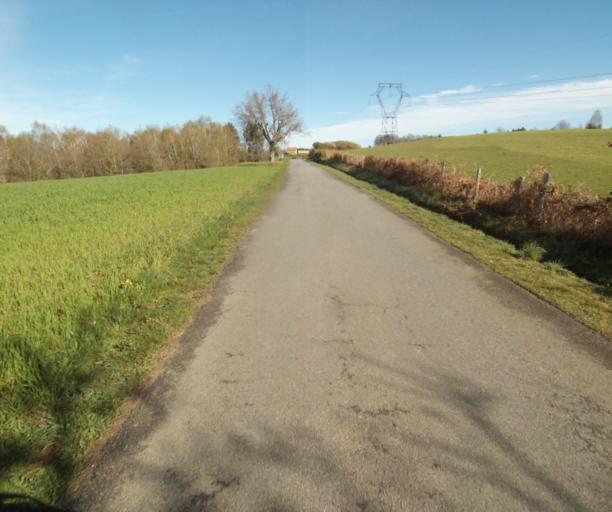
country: FR
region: Limousin
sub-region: Departement de la Correze
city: Laguenne
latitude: 45.2619
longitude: 1.8564
